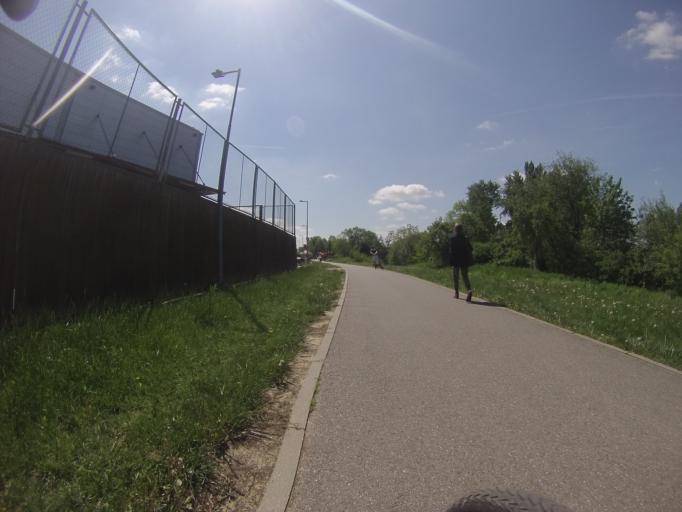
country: CZ
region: South Moravian
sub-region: Mesto Brno
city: Brno
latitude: 49.1571
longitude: 16.6257
